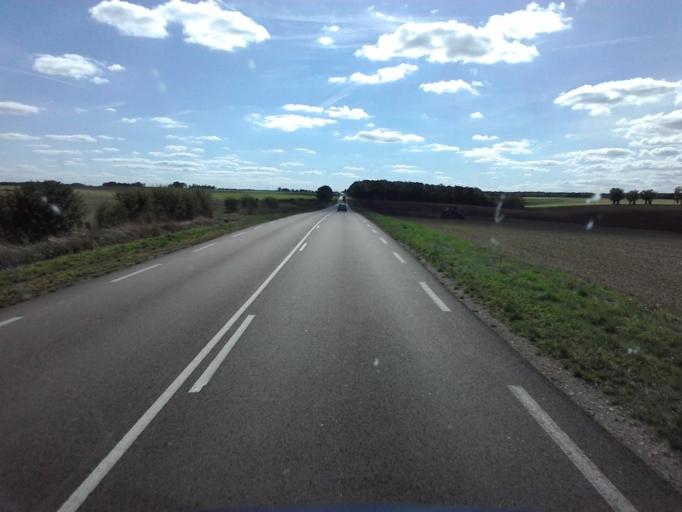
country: FR
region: Bourgogne
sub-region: Departement de la Cote-d'Or
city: Chatillon-sur-Seine
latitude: 47.8427
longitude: 4.5520
